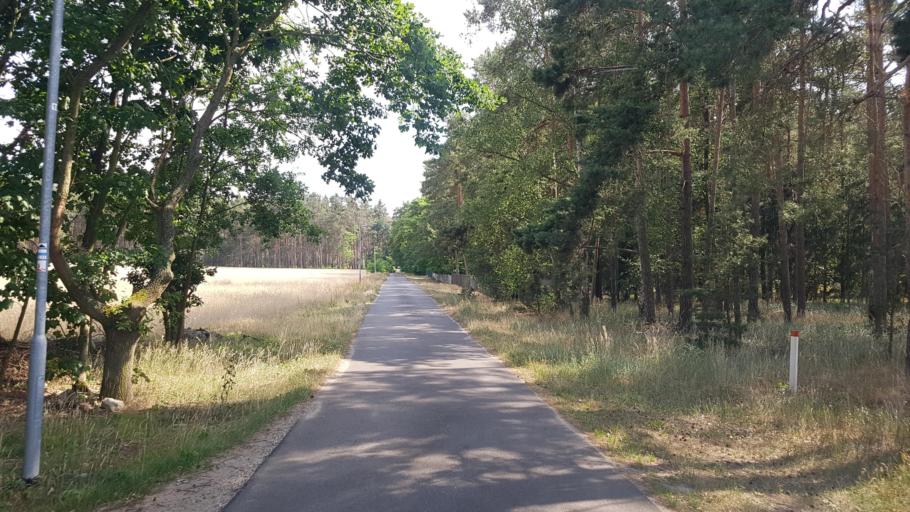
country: DE
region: Brandenburg
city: Belzig
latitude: 52.1936
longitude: 12.6066
